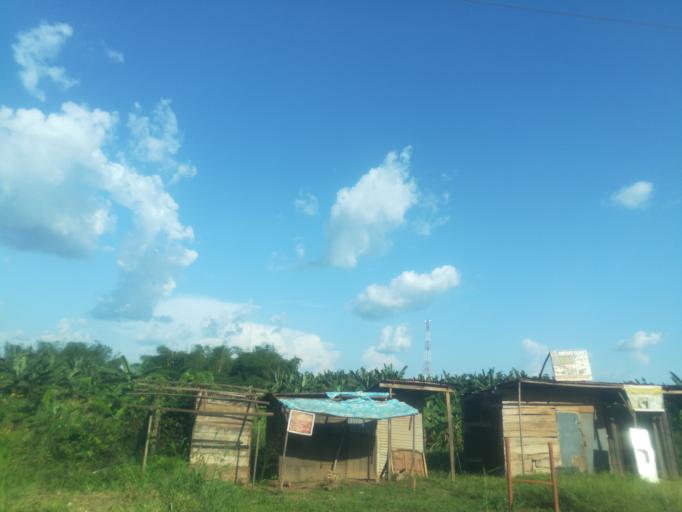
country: NG
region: Oyo
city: Egbeda
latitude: 7.4271
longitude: 3.9859
